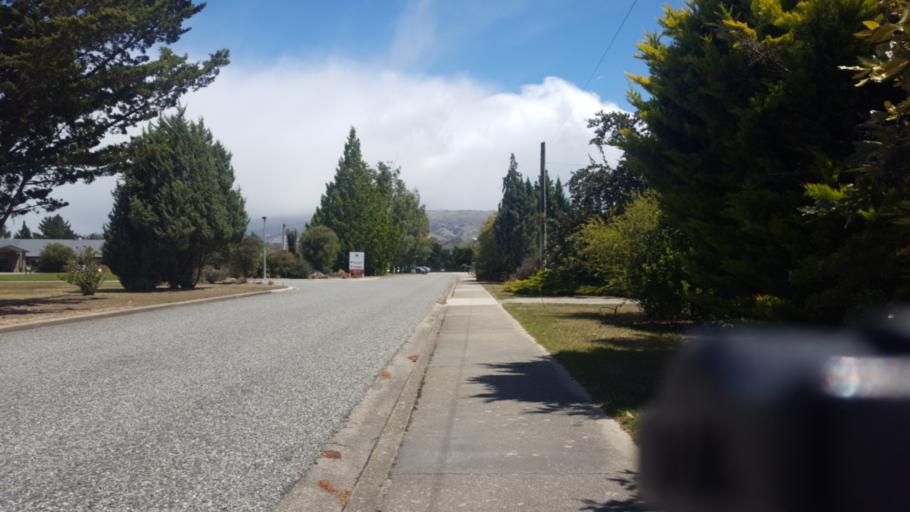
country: NZ
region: Otago
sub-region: Queenstown-Lakes District
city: Wanaka
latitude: -45.1995
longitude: 169.3313
